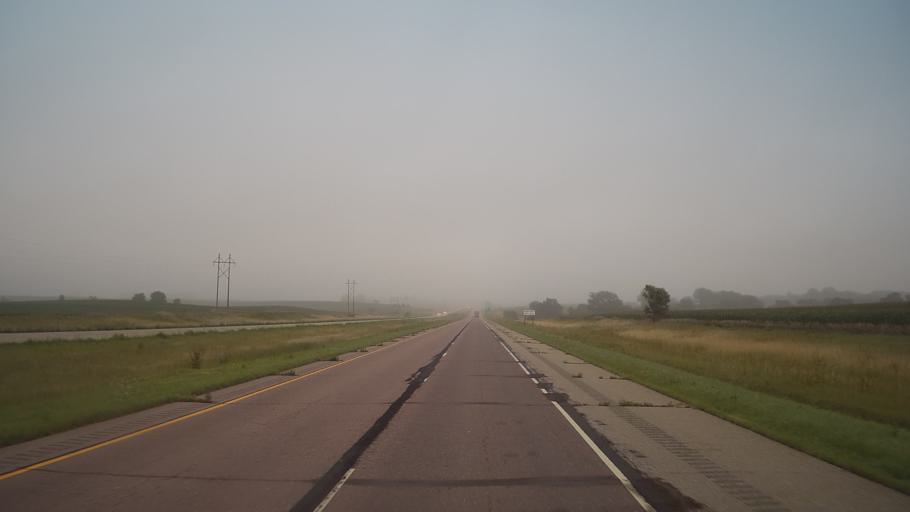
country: US
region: Minnesota
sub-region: Martin County
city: Fairmont
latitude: 43.6804
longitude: -94.5223
